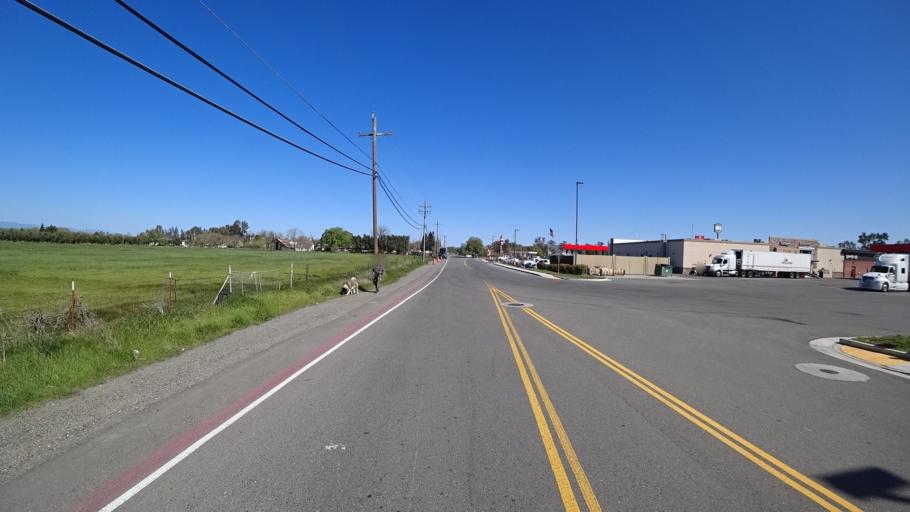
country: US
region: California
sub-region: Glenn County
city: Orland
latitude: 39.7503
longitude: -122.2090
